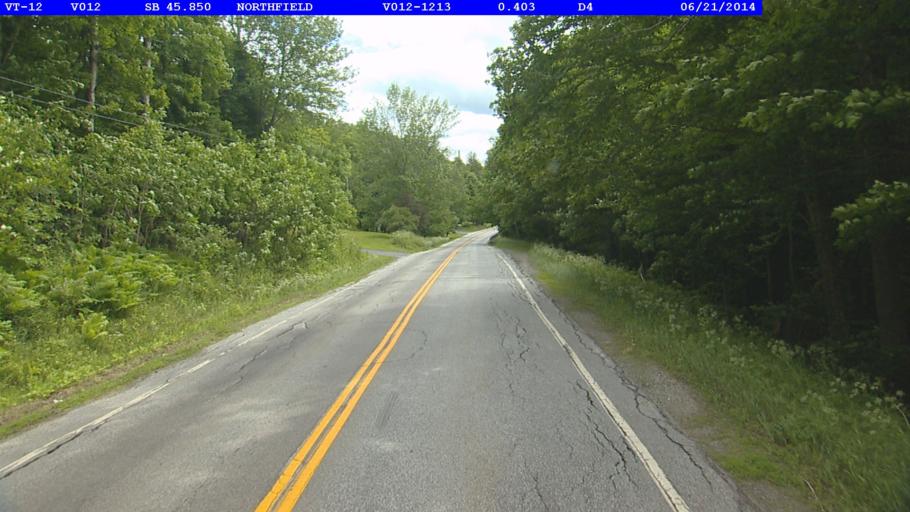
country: US
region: Vermont
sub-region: Washington County
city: Northfield
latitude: 44.0982
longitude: -72.6444
